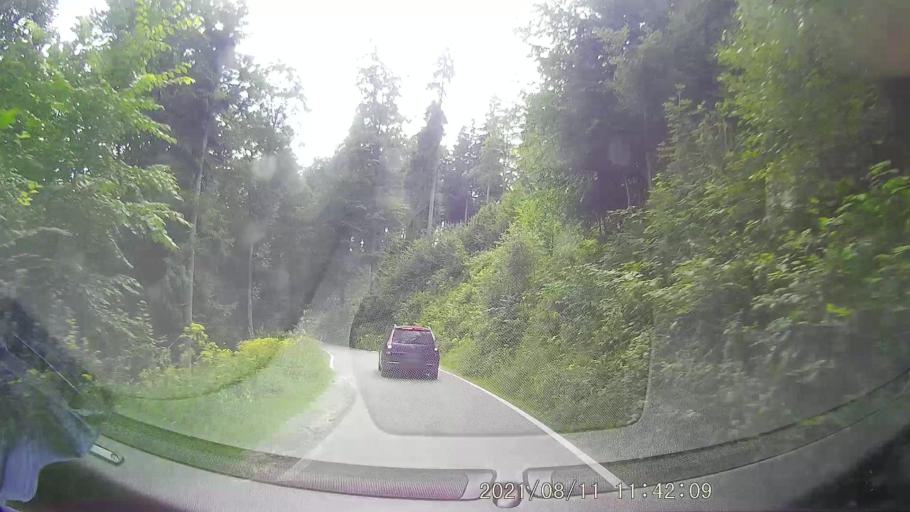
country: PL
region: Lower Silesian Voivodeship
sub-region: Powiat klodzki
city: Stronie Slaskie
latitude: 50.2517
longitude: 16.8402
